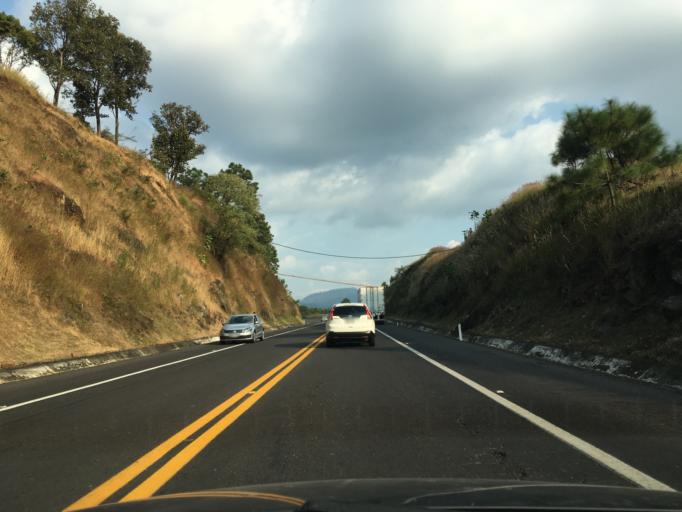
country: MX
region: Michoacan
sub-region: Ziracuaretiro
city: Patuan
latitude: 19.4324
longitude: -101.8968
